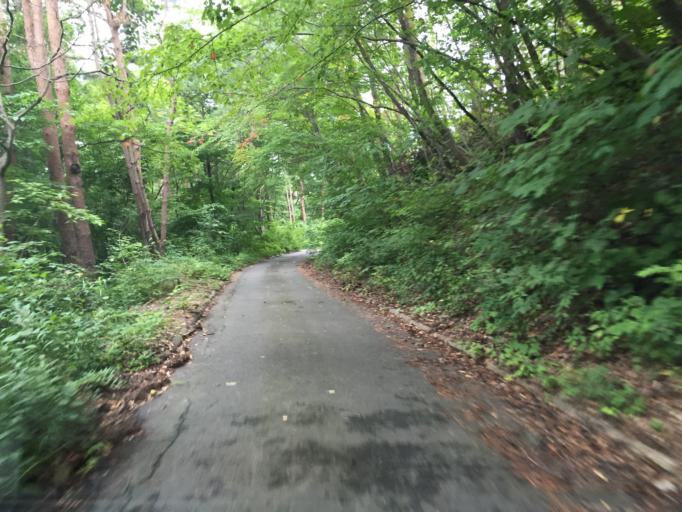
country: JP
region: Fukushima
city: Motomiya
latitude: 37.5544
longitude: 140.3009
